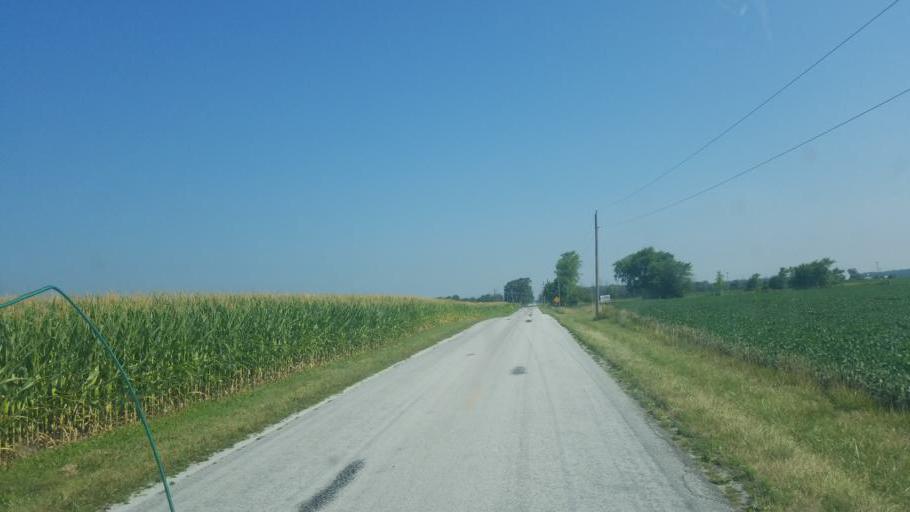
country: US
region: Ohio
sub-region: Hardin County
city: Kenton
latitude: 40.6684
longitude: -83.5380
